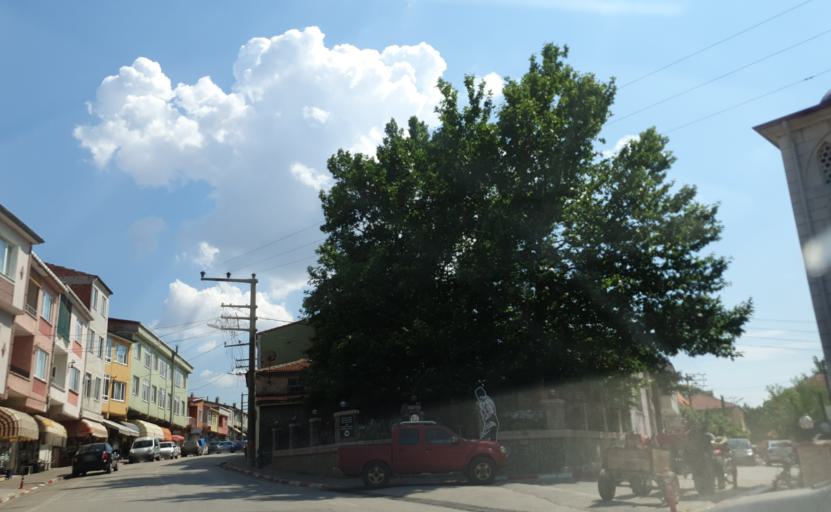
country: TR
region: Kirklareli
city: Buyukkaristiran
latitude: 41.4403
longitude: 27.5856
